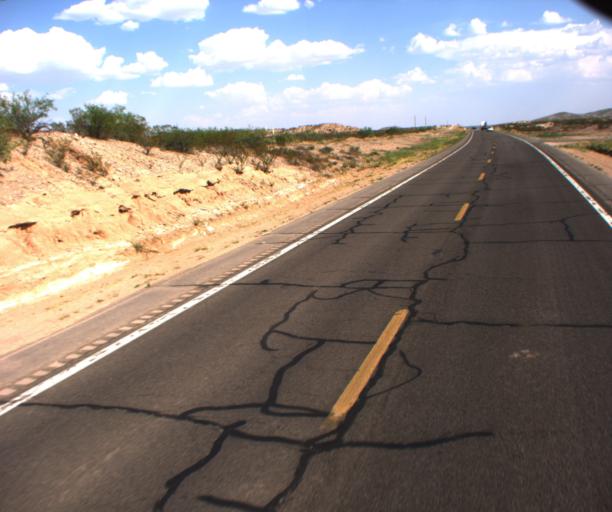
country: US
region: Arizona
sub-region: Greenlee County
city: Clifton
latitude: 32.7824
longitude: -109.1584
